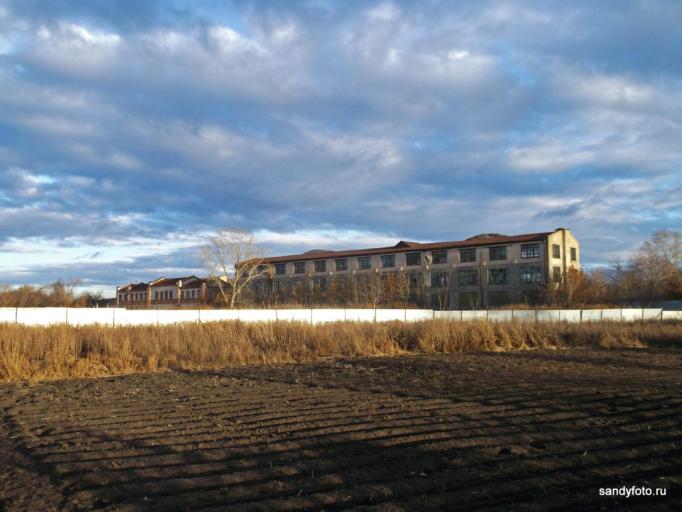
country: RU
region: Chelyabinsk
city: Troitsk
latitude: 54.0841
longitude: 61.5781
